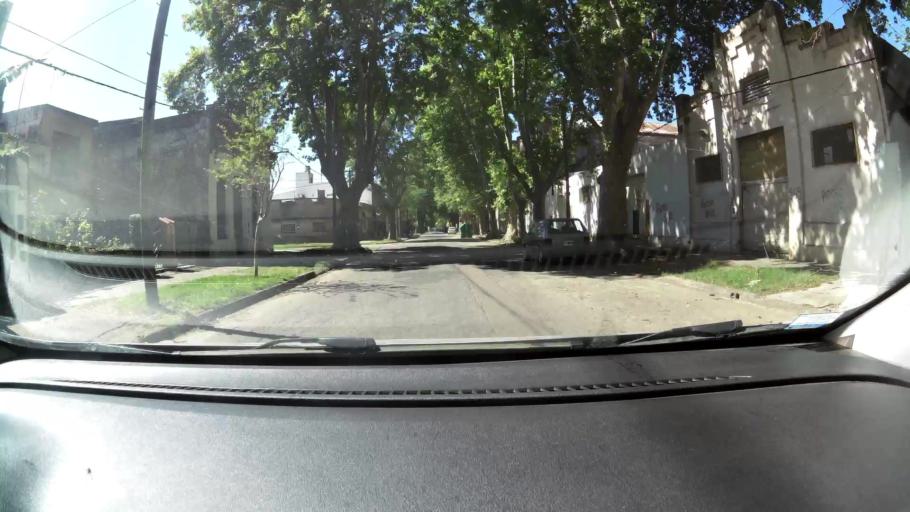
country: AR
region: Santa Fe
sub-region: Departamento de Rosario
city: Rosario
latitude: -32.9388
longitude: -60.6935
